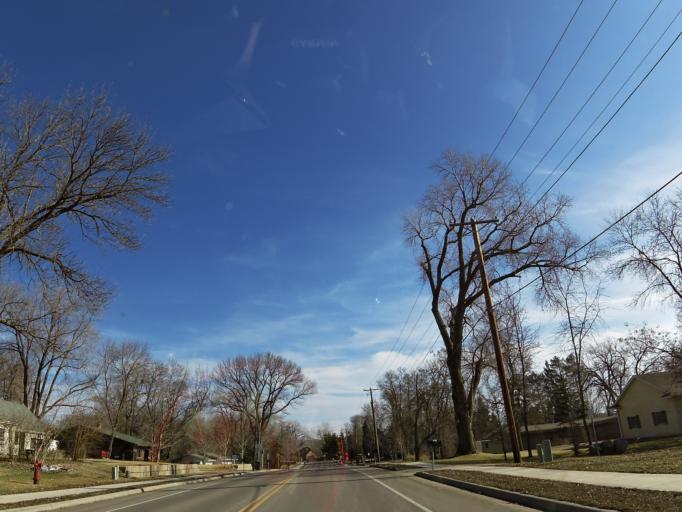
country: US
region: Minnesota
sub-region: Scott County
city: Prior Lake
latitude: 44.7050
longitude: -93.4617
